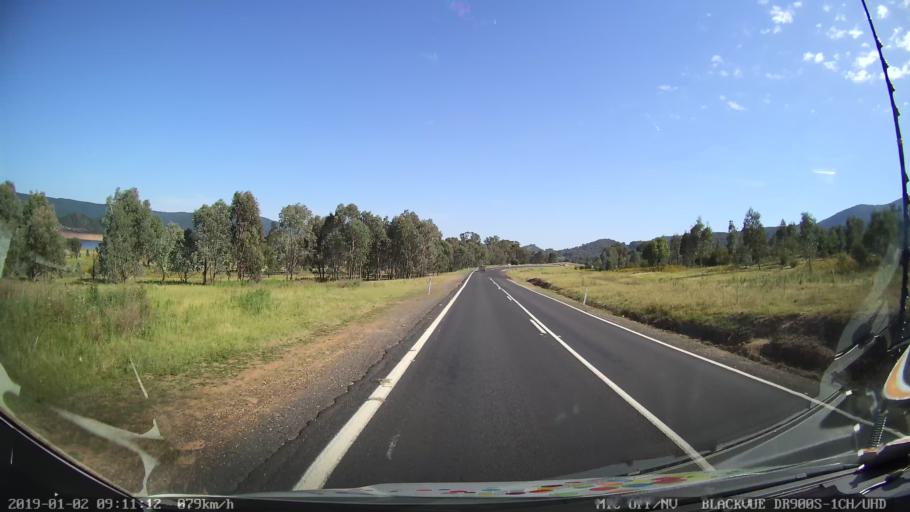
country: AU
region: New South Wales
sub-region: Tumut Shire
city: Tumut
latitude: -35.5137
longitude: 148.2688
